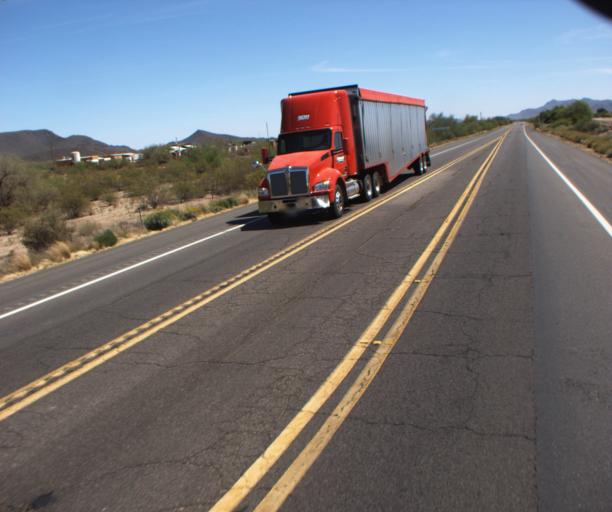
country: US
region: Arizona
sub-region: Pinal County
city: Sacaton
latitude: 33.1335
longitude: -111.7518
